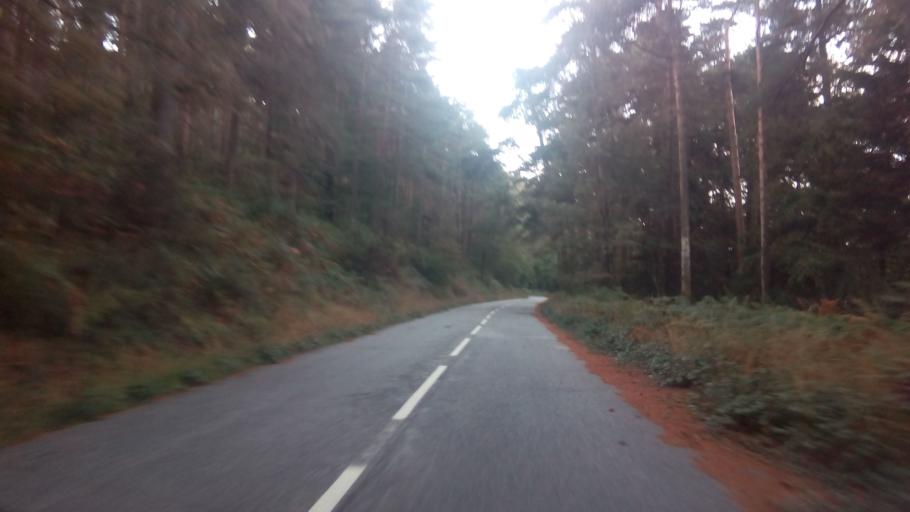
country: PT
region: Vila Real
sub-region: Mesao Frio
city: Mesao Frio
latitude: 41.2795
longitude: -7.9173
